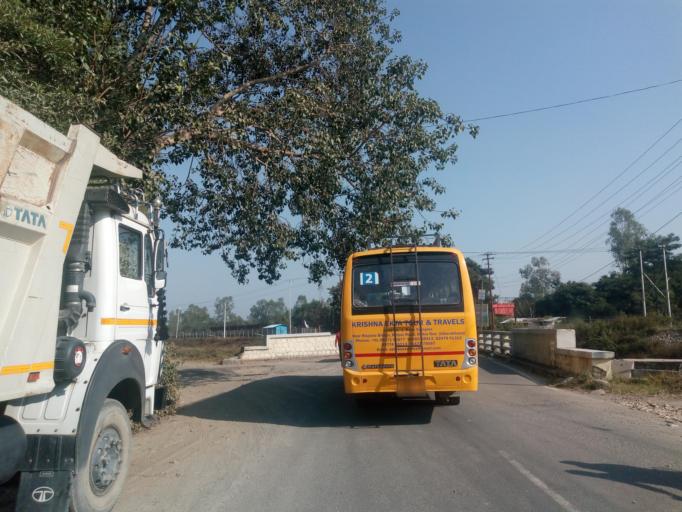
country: IN
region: Uttarakhand
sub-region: Dehradun
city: Harbatpur
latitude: 30.4427
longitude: 77.7034
